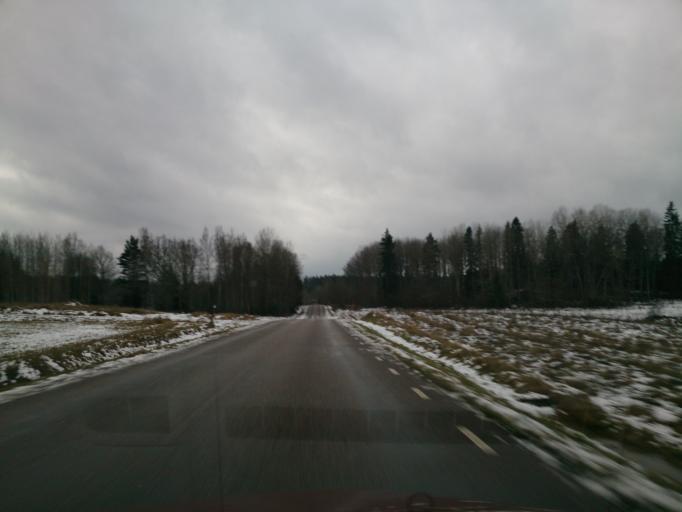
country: SE
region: OEstergoetland
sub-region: Atvidabergs Kommun
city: Atvidaberg
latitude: 58.2792
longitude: 16.0346
